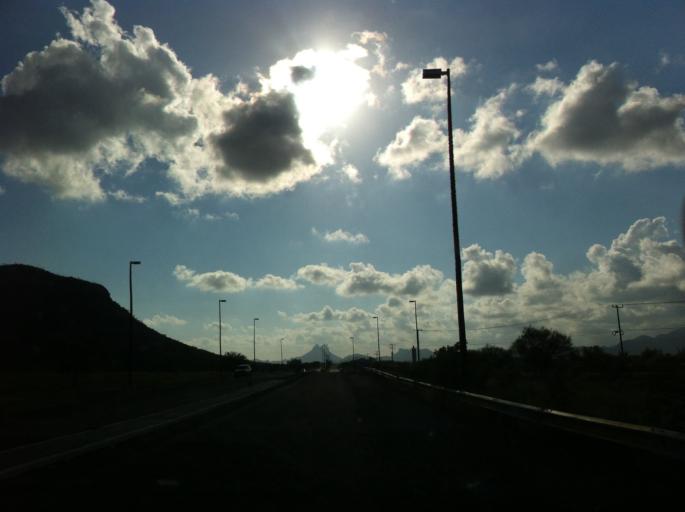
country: MX
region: Sonora
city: Heroica Guaymas
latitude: 27.9873
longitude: -110.9426
